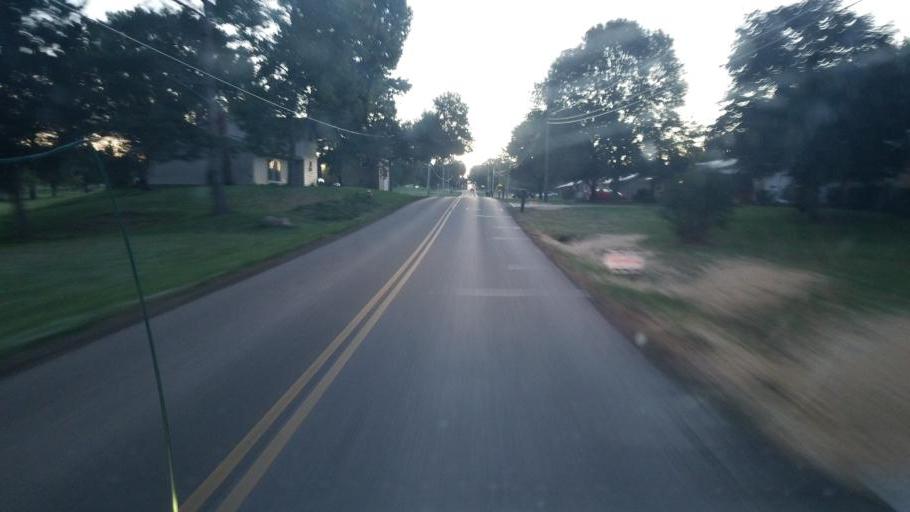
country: US
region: Ohio
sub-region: Wayne County
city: Apple Creek
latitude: 40.7409
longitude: -81.8198
